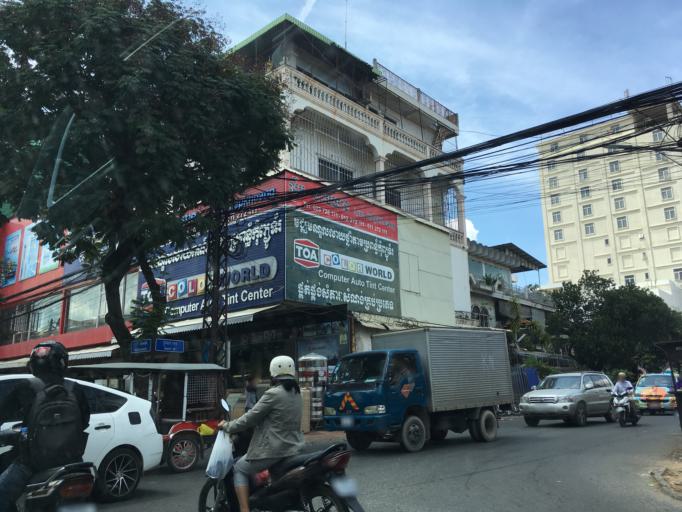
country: KH
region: Phnom Penh
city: Phnom Penh
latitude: 11.5439
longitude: 104.9166
